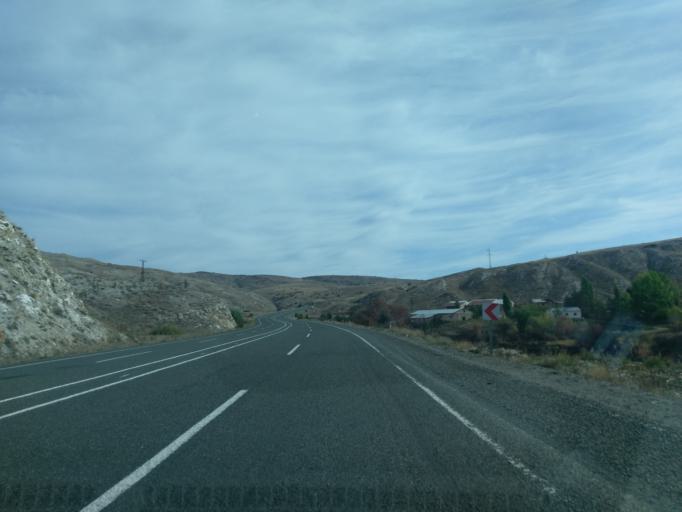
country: TR
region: Sivas
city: Zara
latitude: 39.8563
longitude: 37.8691
